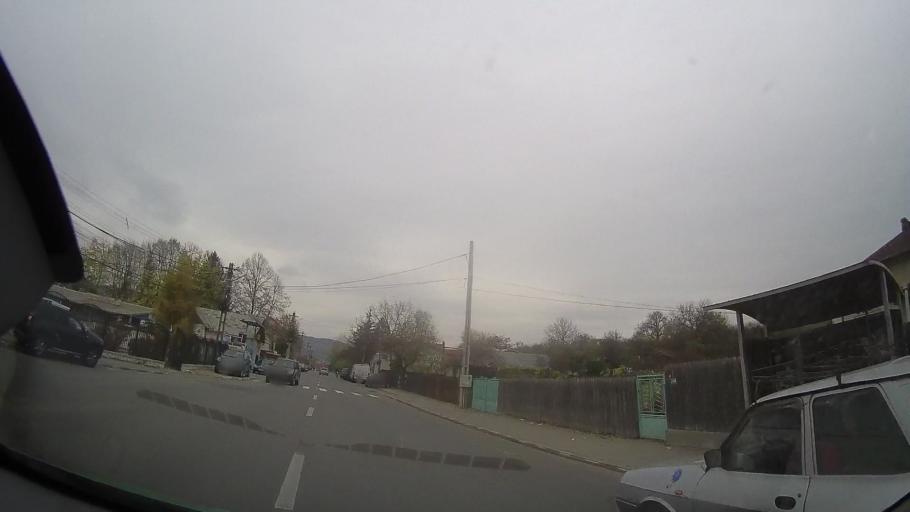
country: RO
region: Prahova
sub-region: Oras Urlati
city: Urlati
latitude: 44.9958
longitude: 26.2306
